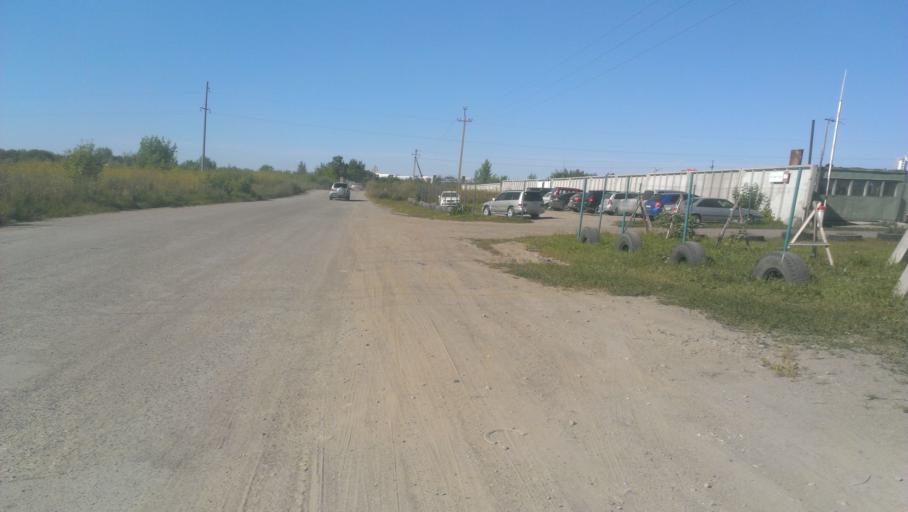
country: RU
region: Altai Krai
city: Novosilikatnyy
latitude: 53.3350
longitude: 83.6352
